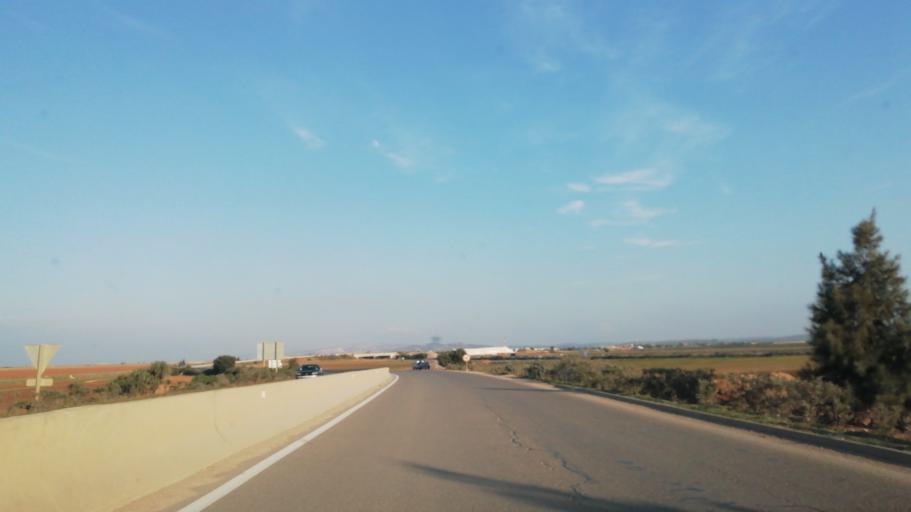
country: DZ
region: Relizane
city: Djidiouia
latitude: 35.8960
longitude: 0.7035
